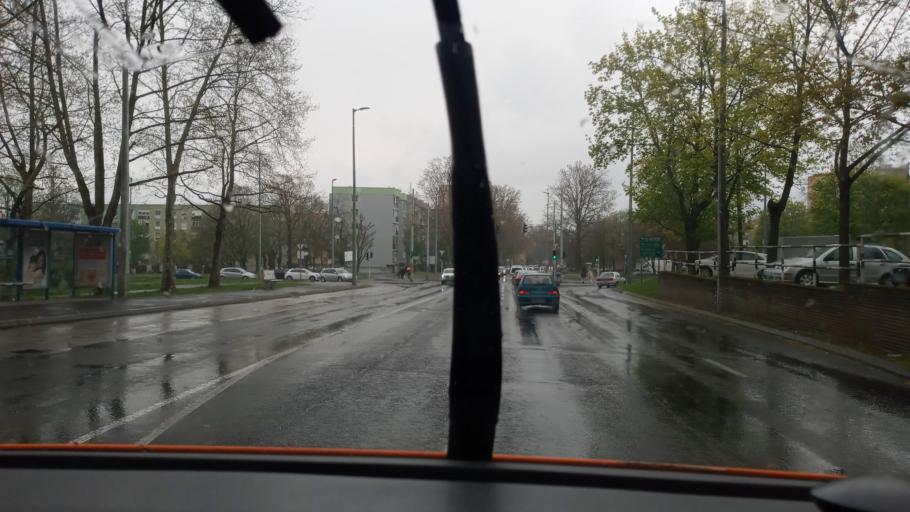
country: HU
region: Baranya
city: Pecs
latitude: 46.0416
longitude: 18.2164
